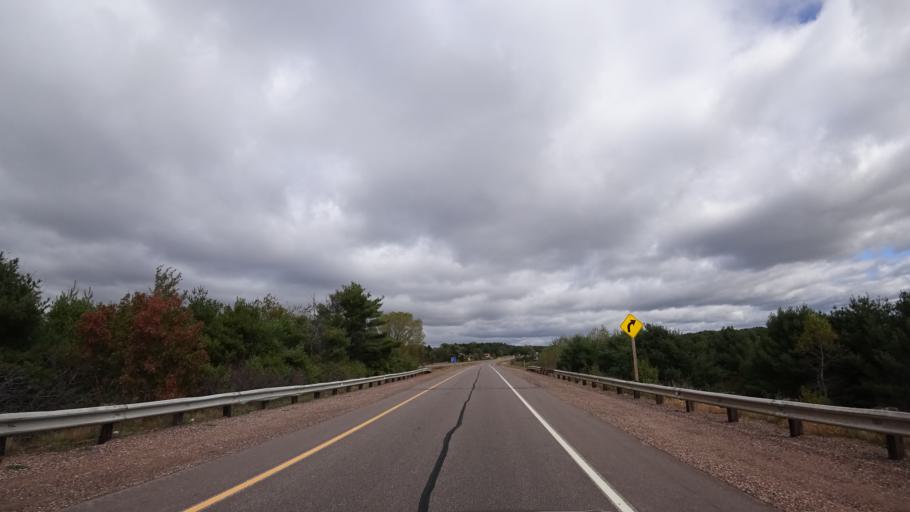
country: US
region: Wisconsin
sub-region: Chippewa County
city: Lake Wissota
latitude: 44.9200
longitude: -91.3358
